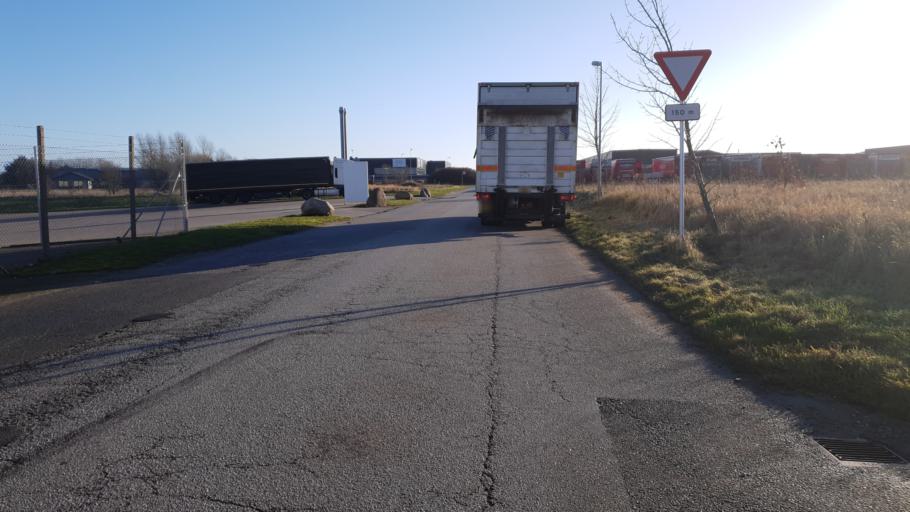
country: DK
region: Central Jutland
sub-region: Hedensted Kommune
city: Hedensted
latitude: 55.7924
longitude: 9.6736
